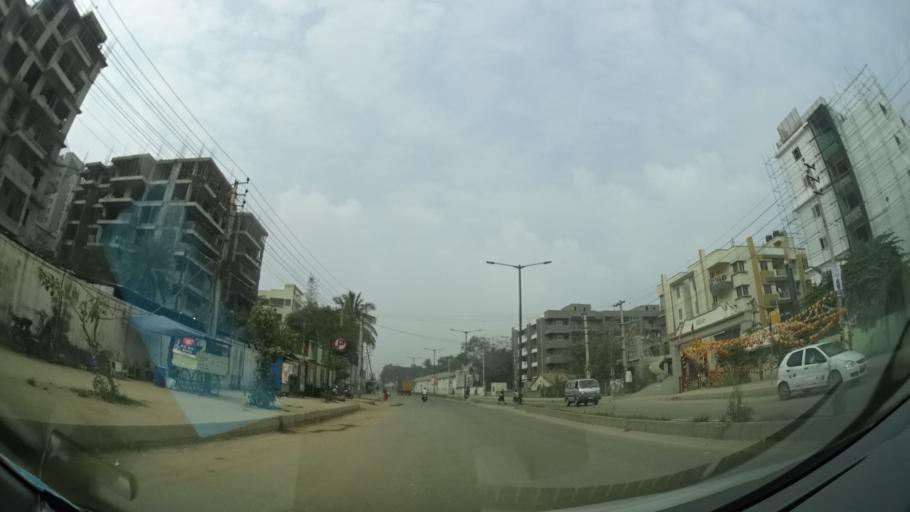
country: IN
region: Karnataka
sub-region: Bangalore Rural
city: Hoskote
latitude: 12.9832
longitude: 77.7550
